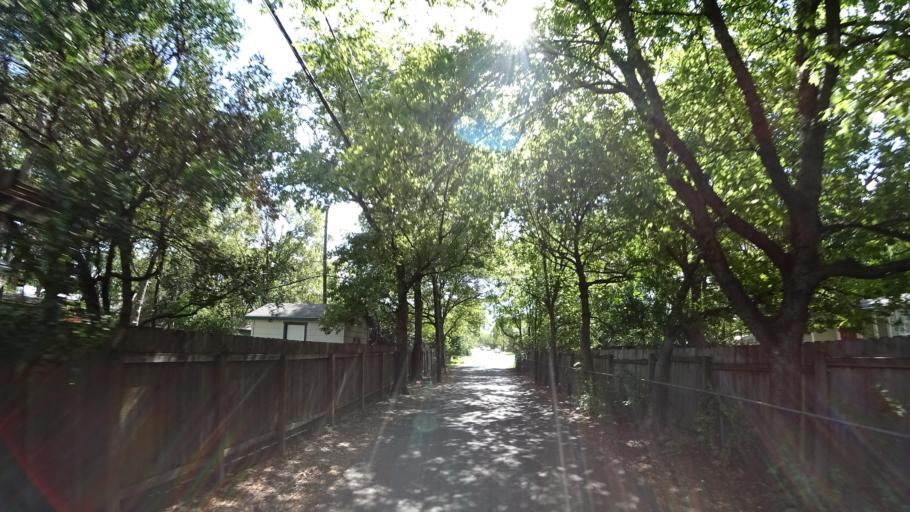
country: US
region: Texas
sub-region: Travis County
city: Austin
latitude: 30.3487
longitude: -97.7312
